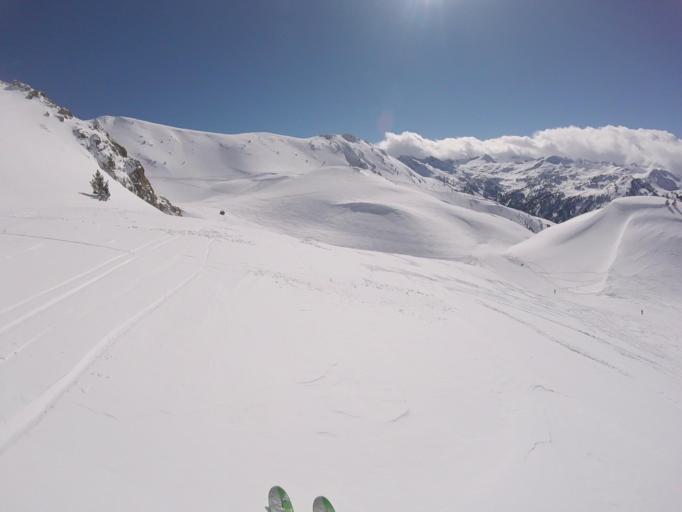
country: ES
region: Catalonia
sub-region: Provincia de Lleida
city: Espot
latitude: 42.6744
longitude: 0.9894
